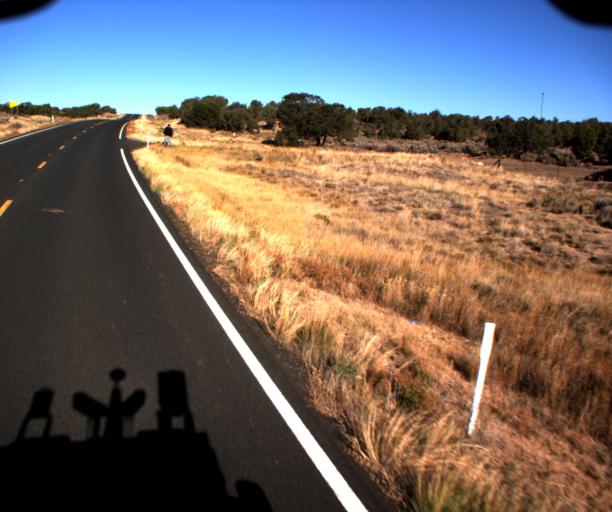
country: US
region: Arizona
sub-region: Apache County
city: Ganado
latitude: 35.7624
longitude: -109.7842
